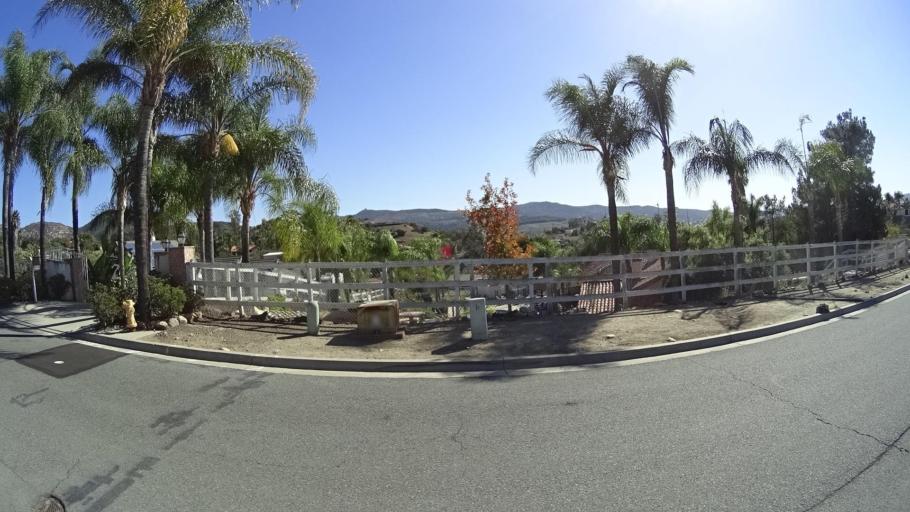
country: US
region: California
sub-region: San Diego County
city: Lakeside
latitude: 32.8555
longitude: -116.8775
